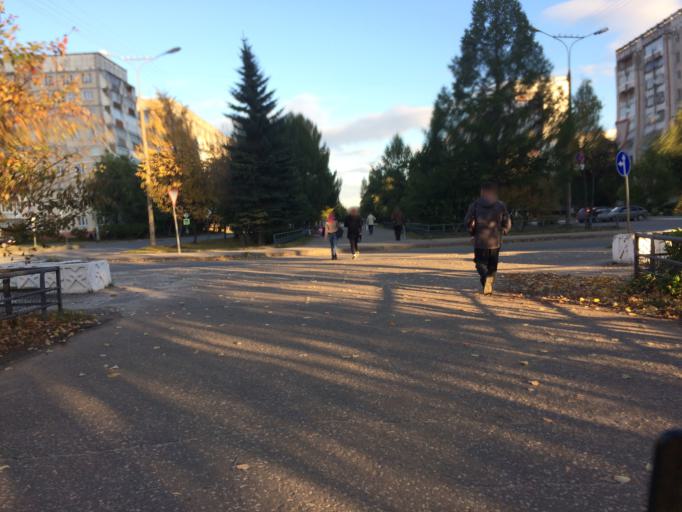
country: RU
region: Mariy-El
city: Yoshkar-Ola
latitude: 56.6320
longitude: 47.9114
